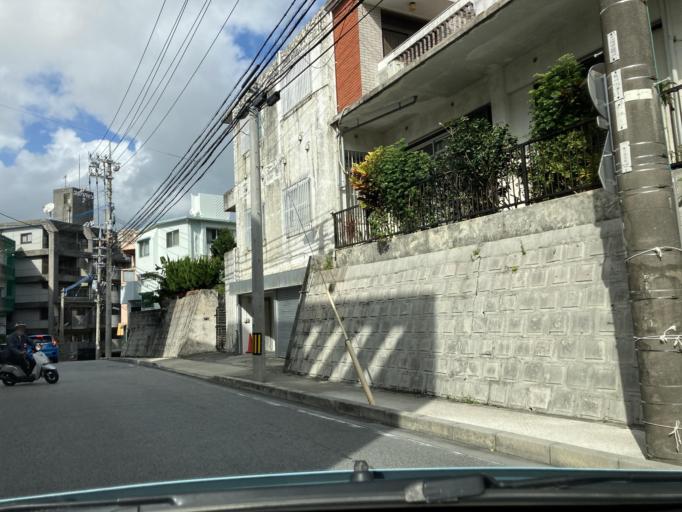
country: JP
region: Okinawa
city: Naha-shi
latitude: 26.2138
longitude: 127.7089
